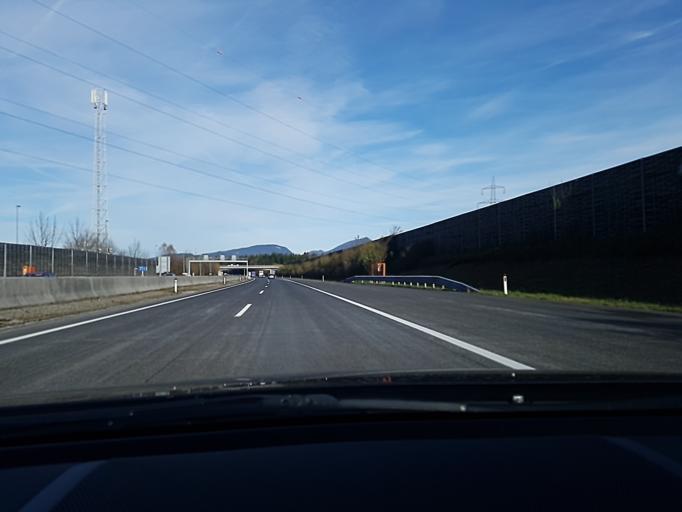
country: AT
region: Salzburg
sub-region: Politischer Bezirk Hallein
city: Kuchl
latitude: 47.6491
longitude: 13.1369
